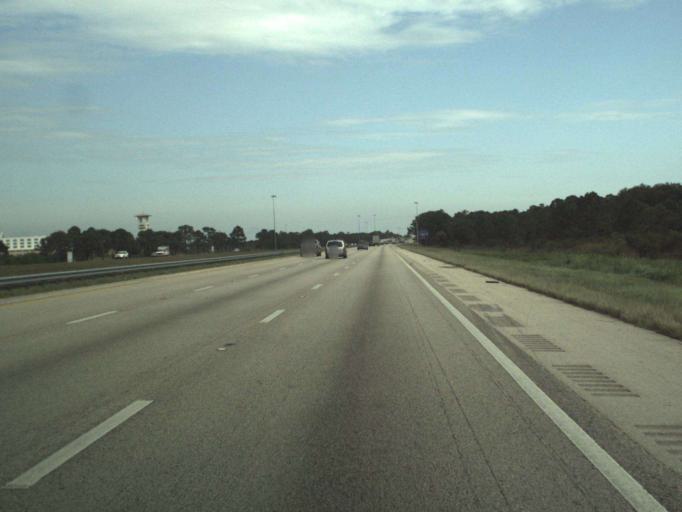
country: US
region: Florida
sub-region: Saint Lucie County
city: Port Saint Lucie
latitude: 27.2521
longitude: -80.4169
